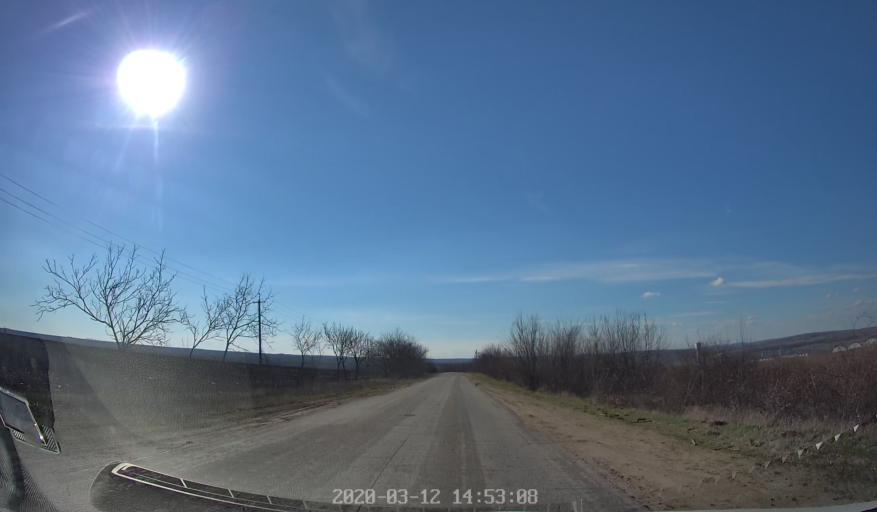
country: MD
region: Criuleni
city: Criuleni
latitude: 47.2191
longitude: 29.0853
